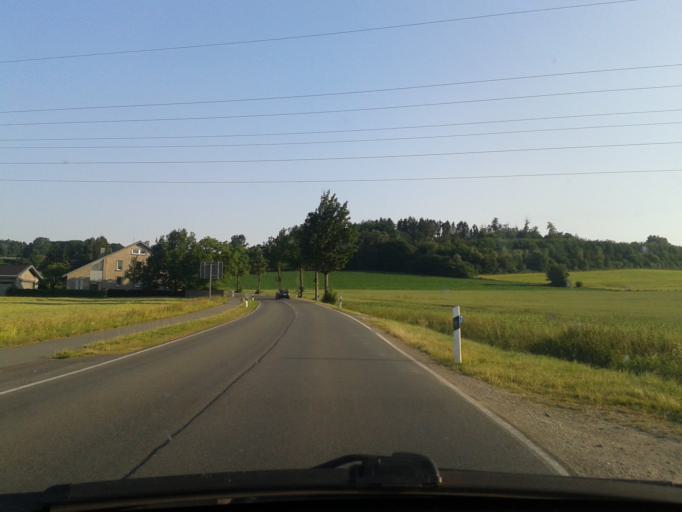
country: DE
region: North Rhine-Westphalia
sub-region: Regierungsbezirk Detmold
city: Detmold
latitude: 51.9685
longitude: 8.9099
